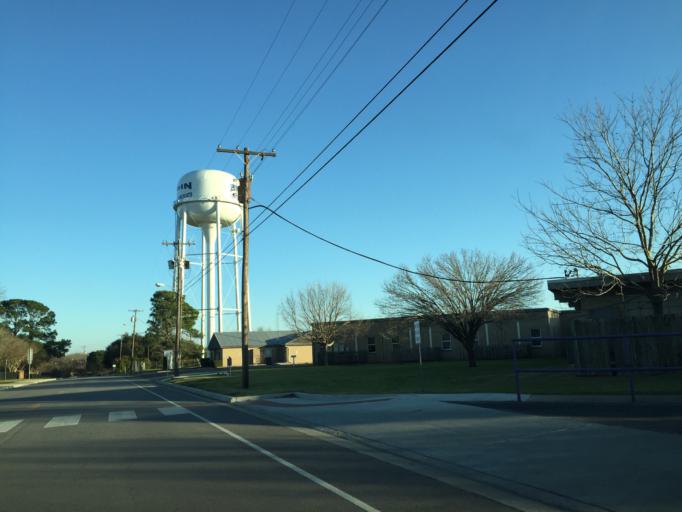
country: US
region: Texas
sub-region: Bastrop County
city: Elgin
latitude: 30.3485
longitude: -97.3792
